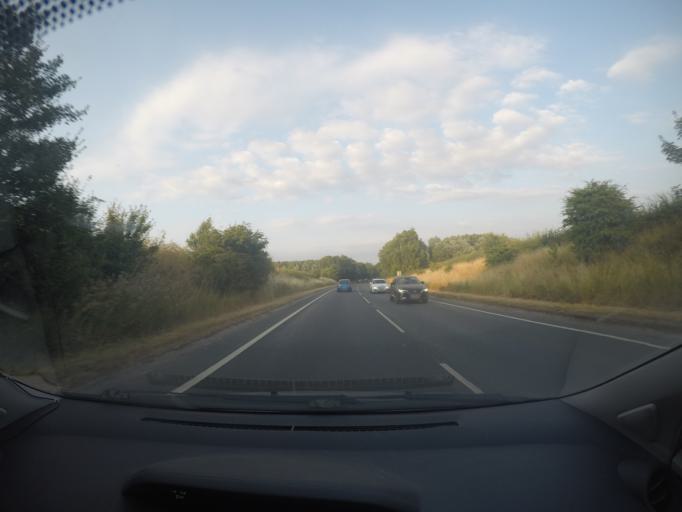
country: GB
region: England
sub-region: City of York
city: Haxby
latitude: 54.0042
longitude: -1.0633
